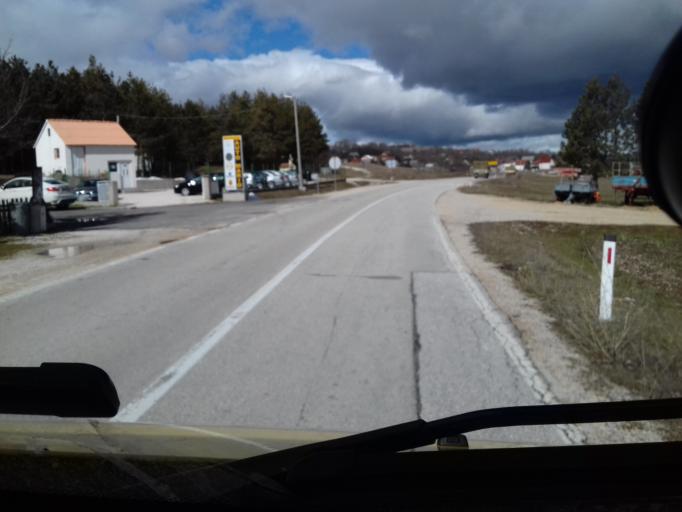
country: BA
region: Federation of Bosnia and Herzegovina
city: Dreznica
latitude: 43.5902
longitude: 17.2742
